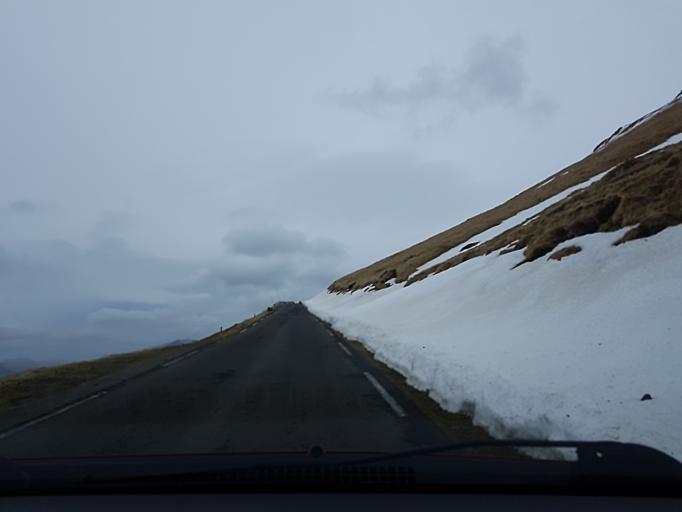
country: FO
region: Streymoy
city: Kollafjordhur
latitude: 62.0025
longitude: -6.9037
